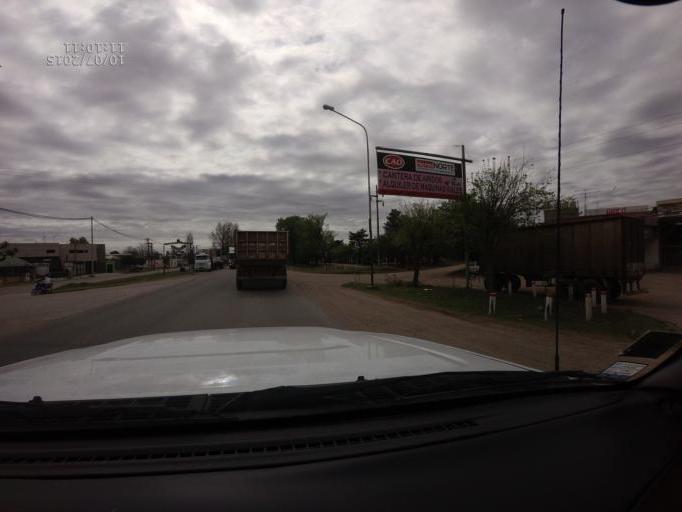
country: AR
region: Cordoba
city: Jesus Maria
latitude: -30.9904
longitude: -64.0966
